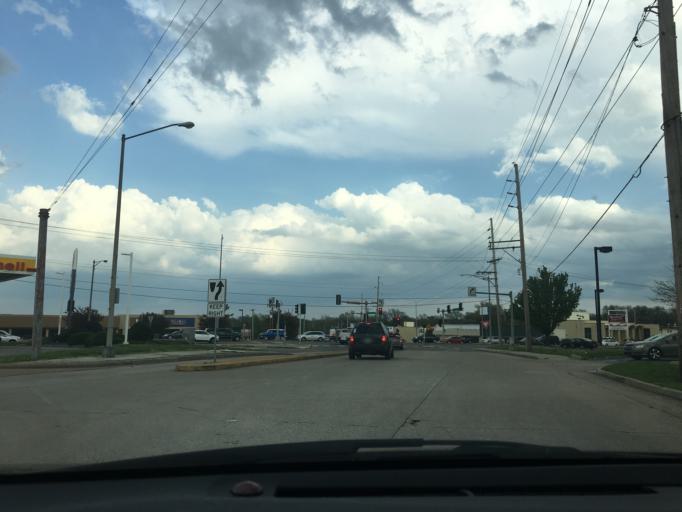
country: US
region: Missouri
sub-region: Saint Louis County
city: Saint Ann
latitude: 38.7318
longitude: -90.4054
